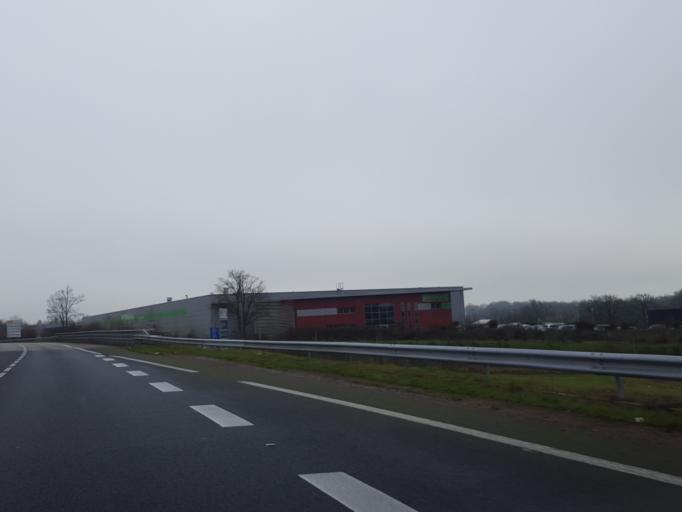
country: FR
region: Pays de la Loire
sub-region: Departement de la Vendee
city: La Ferriere
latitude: 46.6694
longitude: -1.3574
